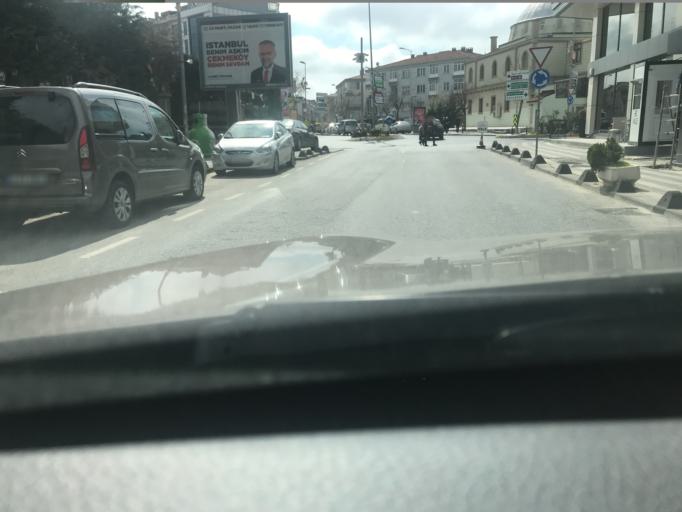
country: TR
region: Istanbul
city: Samandira
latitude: 41.0323
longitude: 29.1815
